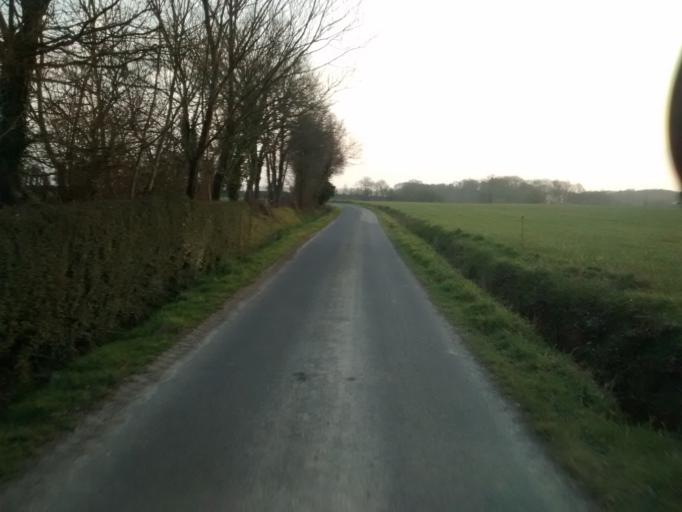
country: FR
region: Brittany
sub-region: Departement du Morbihan
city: Meneac
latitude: 48.1467
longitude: -2.4771
